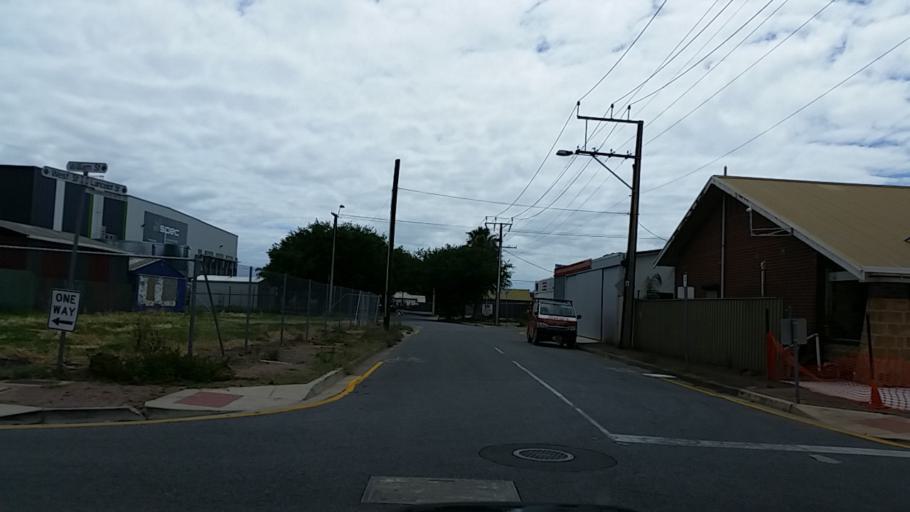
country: AU
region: South Australia
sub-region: Charles Sturt
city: Woodville
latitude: -34.8911
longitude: 138.5469
